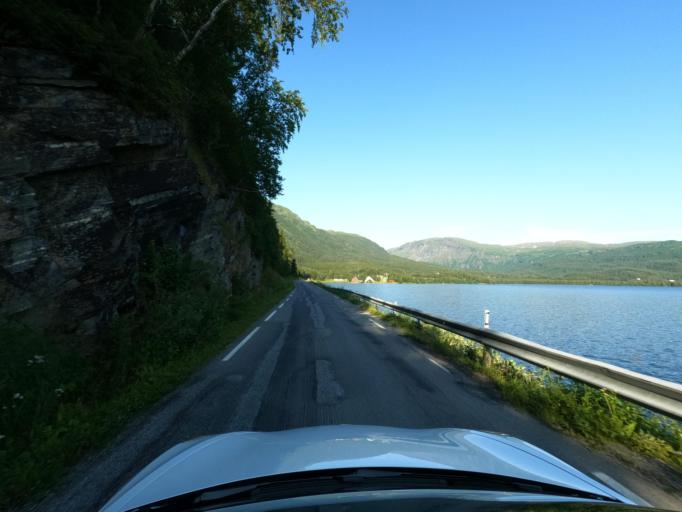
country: NO
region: Troms
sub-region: Gratangen
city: Gratangen
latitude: 68.5606
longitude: 17.6775
